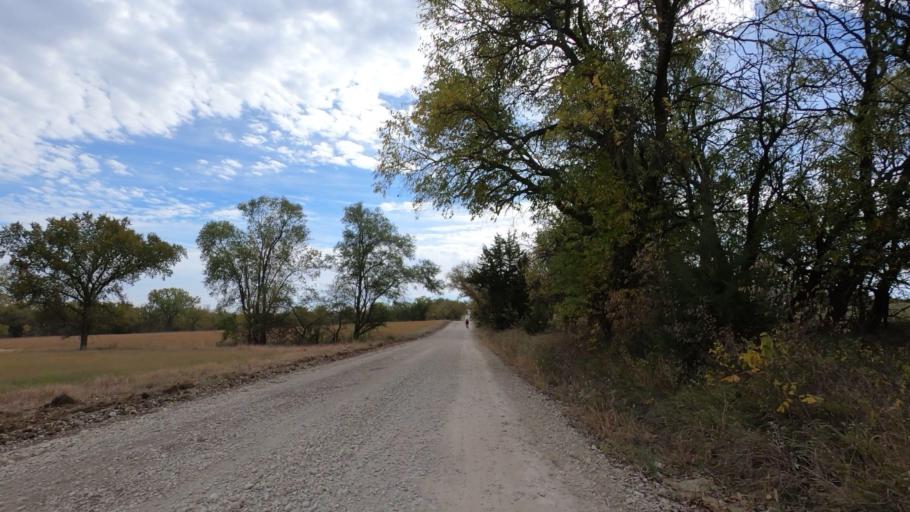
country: US
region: Kansas
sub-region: Pottawatomie County
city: Westmoreland
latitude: 39.3231
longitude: -96.4452
